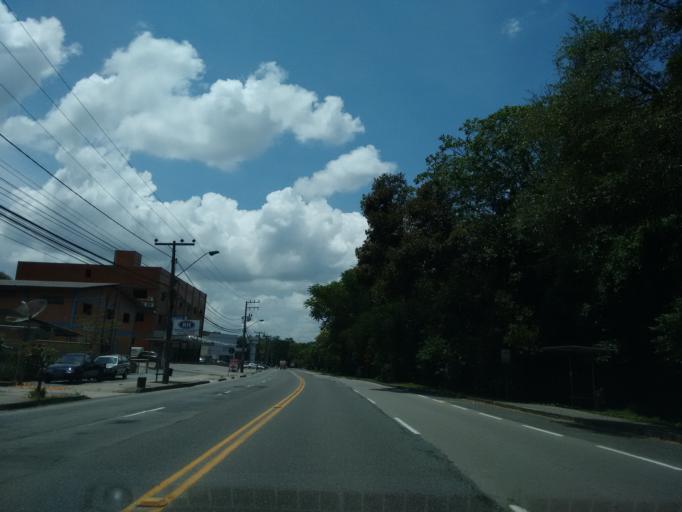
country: BR
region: Santa Catarina
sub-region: Blumenau
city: Blumenau
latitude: -26.9098
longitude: -49.0494
